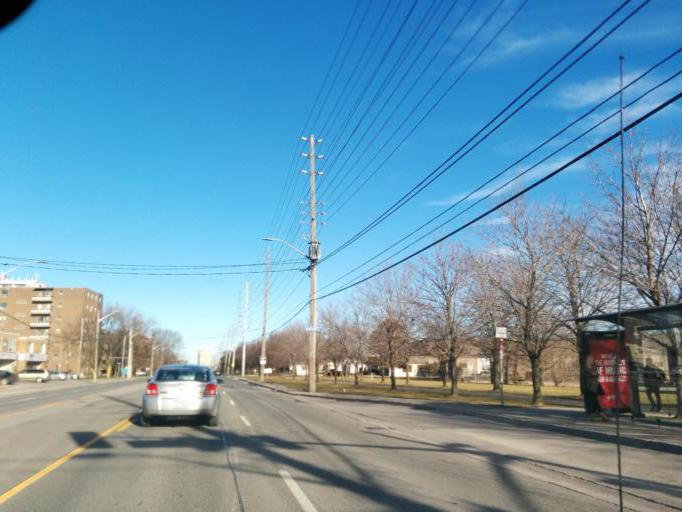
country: CA
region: Ontario
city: Etobicoke
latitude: 43.5799
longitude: -79.5555
